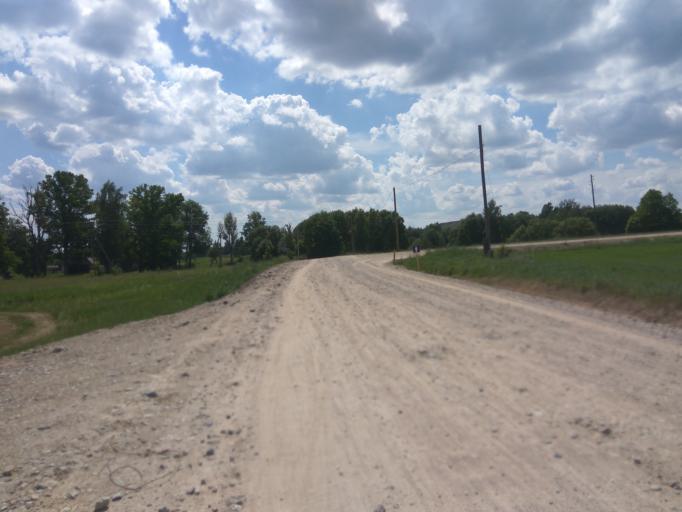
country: LV
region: Kuldigas Rajons
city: Kuldiga
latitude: 56.9046
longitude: 21.9653
